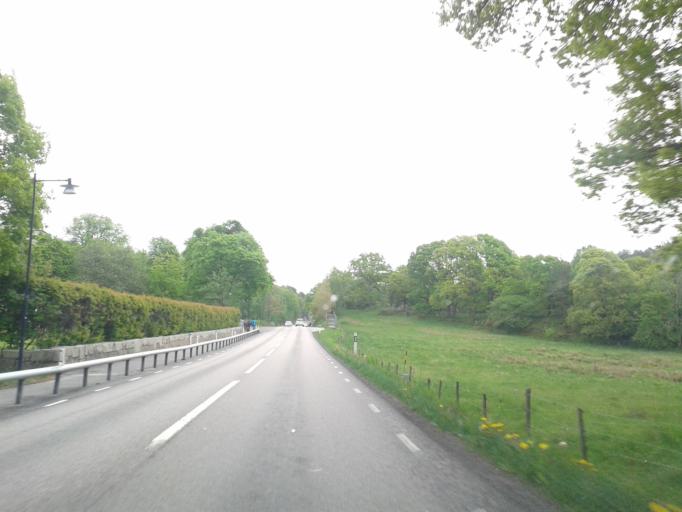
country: SE
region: Vaestra Goetaland
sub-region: Kungalvs Kommun
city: Kode
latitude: 57.8955
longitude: 11.8257
